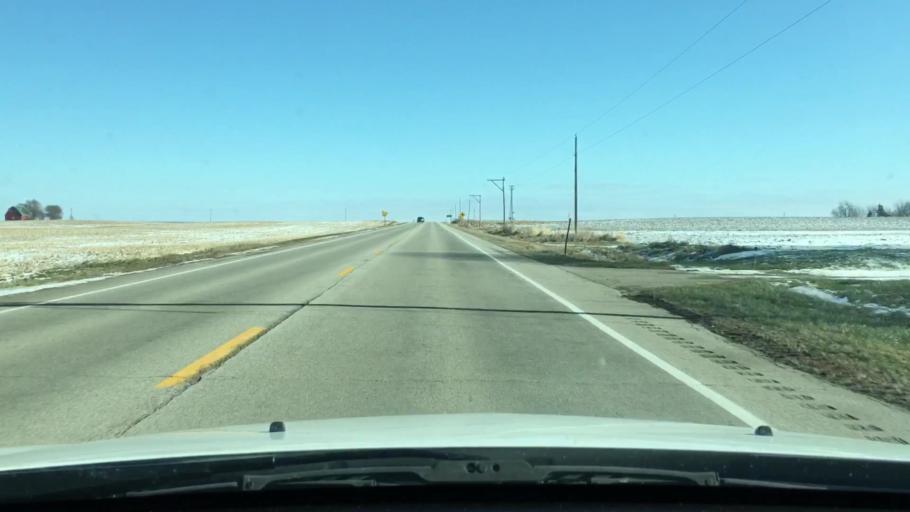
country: US
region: Illinois
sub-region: DeKalb County
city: Malta
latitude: 42.0010
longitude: -88.8845
